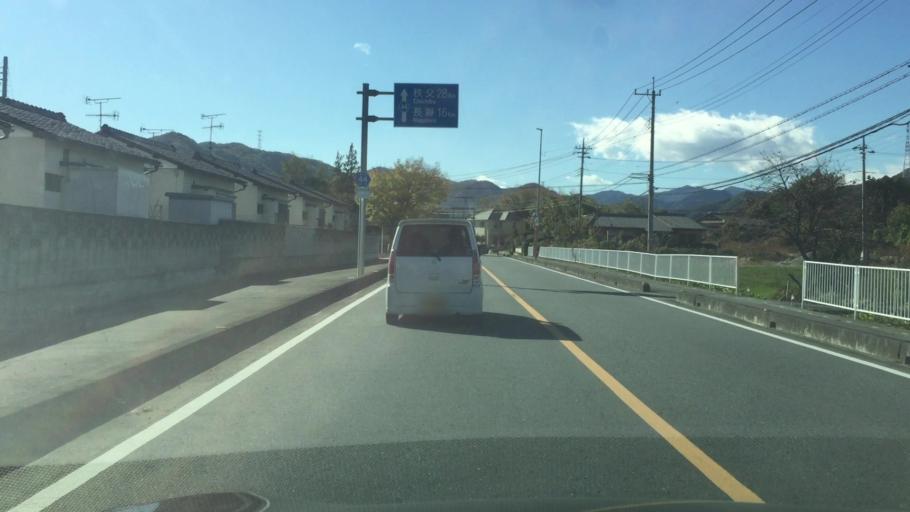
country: JP
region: Saitama
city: Kodamacho-kodamaminami
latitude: 36.1809
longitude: 139.1233
